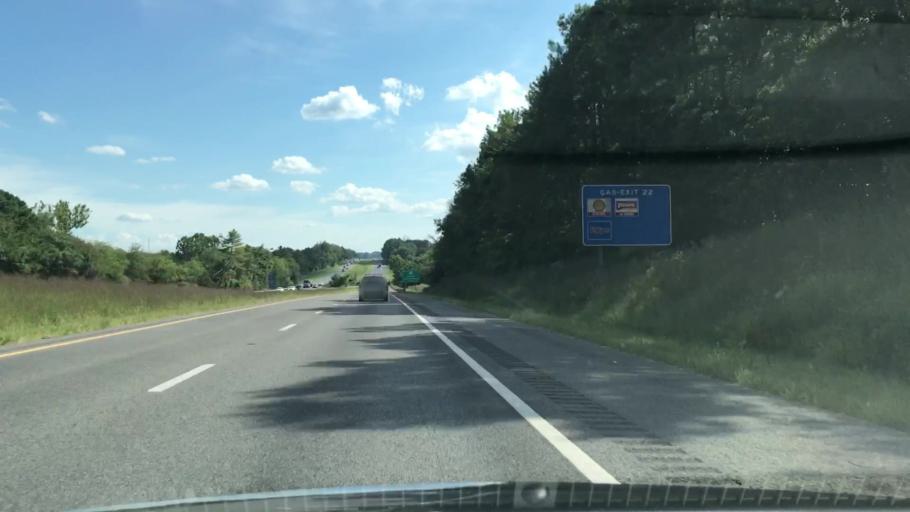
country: US
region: Tennessee
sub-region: Marshall County
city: Cornersville
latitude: 35.3213
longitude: -86.8822
